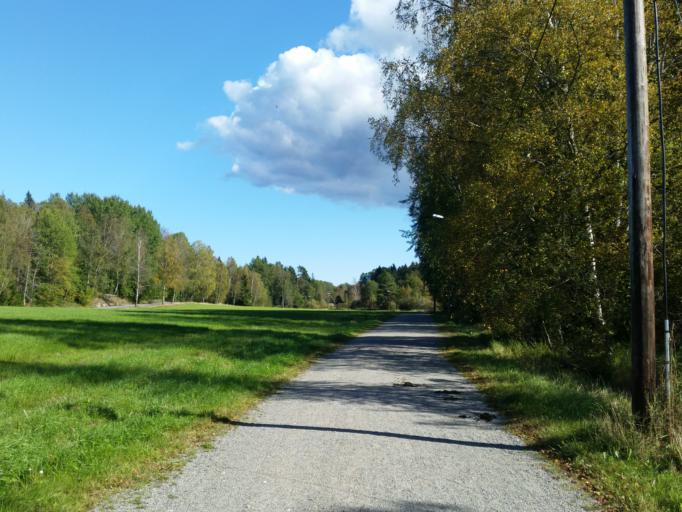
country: SE
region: Stockholm
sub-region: Haninge Kommun
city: Haninge
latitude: 59.1675
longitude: 18.2130
